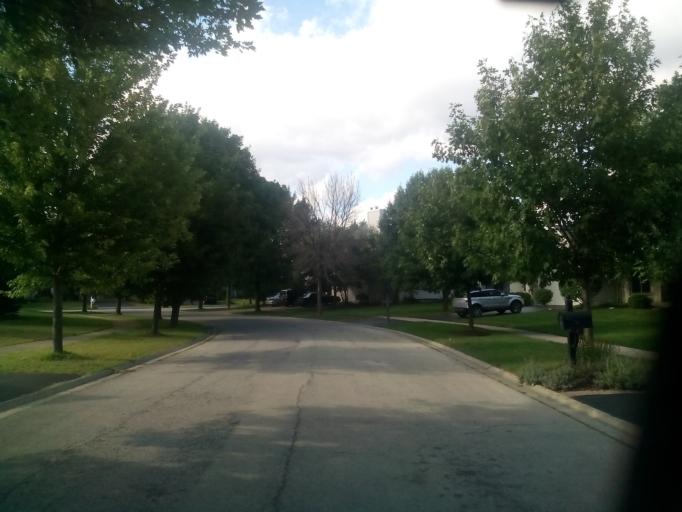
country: US
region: Illinois
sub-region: Will County
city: Romeoville
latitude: 41.6982
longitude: -88.1515
